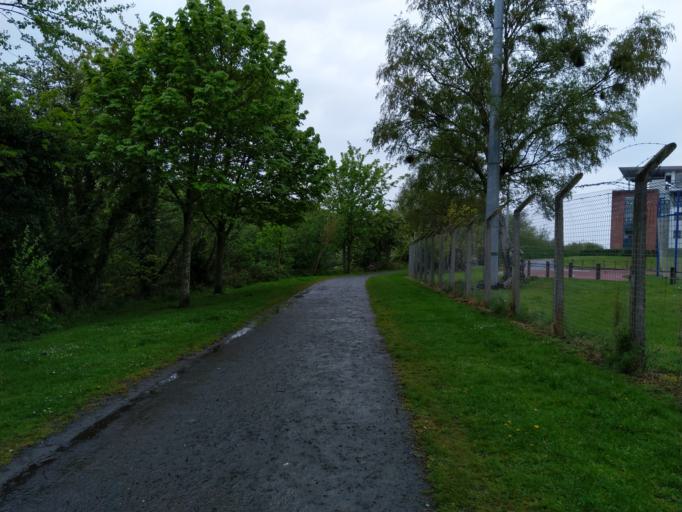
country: GB
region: Scotland
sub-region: South Ayrshire
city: Ayr
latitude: 55.4579
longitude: -4.6191
